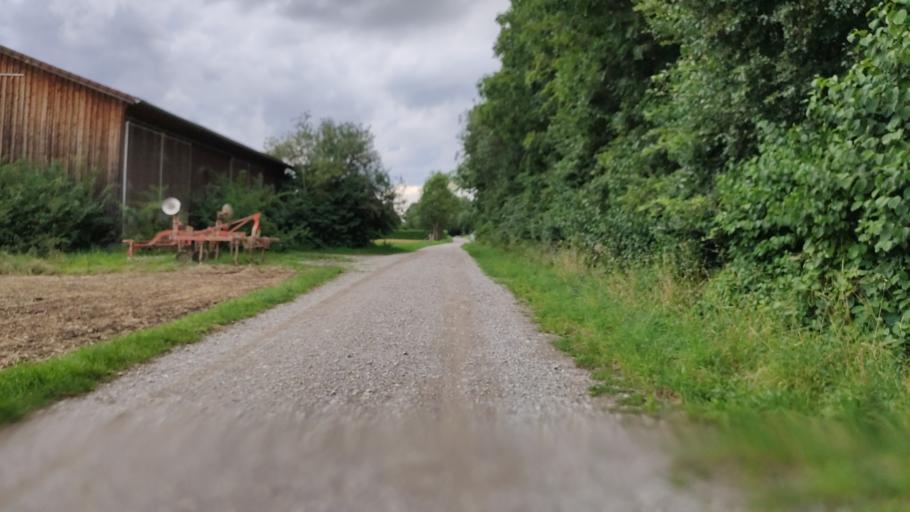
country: DE
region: Bavaria
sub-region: Swabia
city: Oberottmarshausen
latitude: 48.2399
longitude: 10.8633
